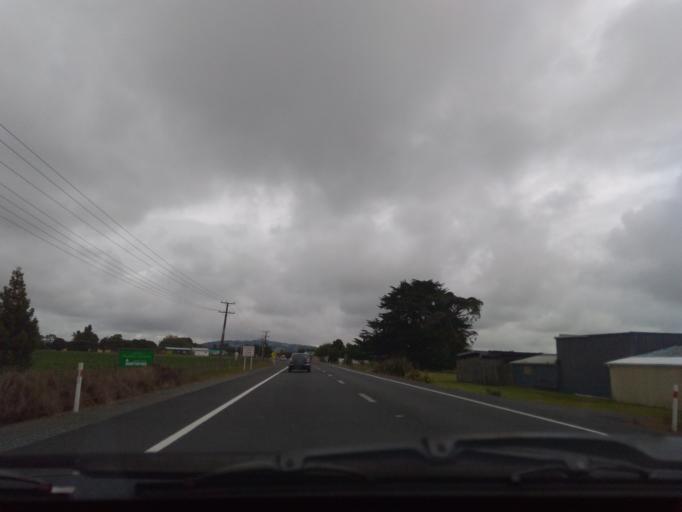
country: NZ
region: Northland
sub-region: Whangarei
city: Ruakaka
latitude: -35.9011
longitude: 174.4439
